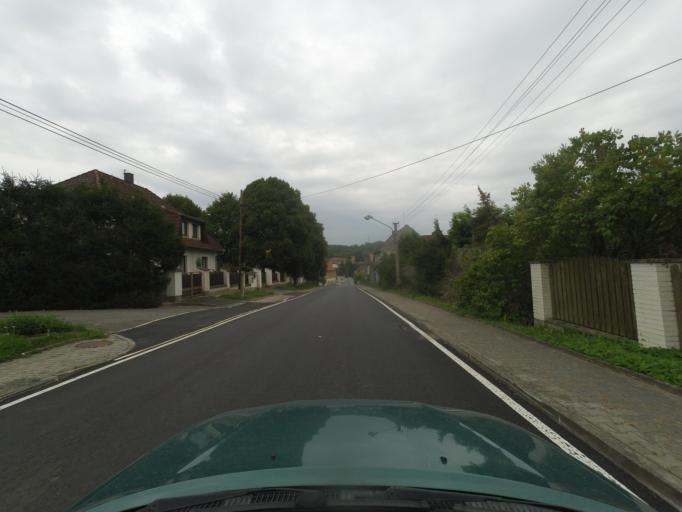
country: CZ
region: Plzensky
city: Merklin
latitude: 49.5585
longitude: 13.1935
